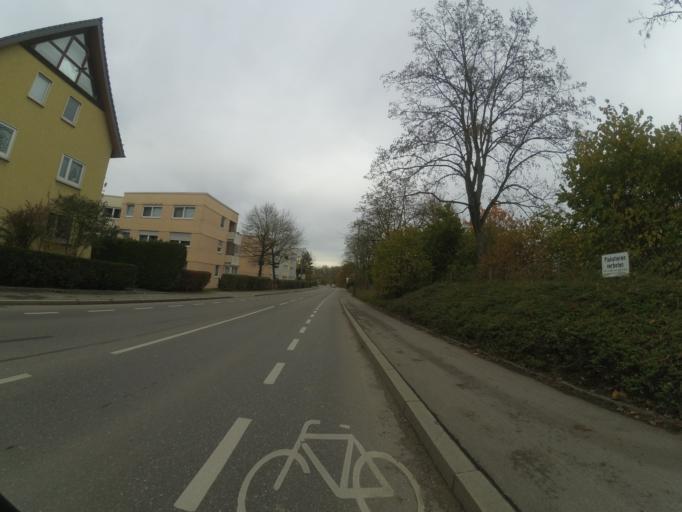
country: DE
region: Baden-Wuerttemberg
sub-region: Tuebingen Region
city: Ulm
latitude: 48.3628
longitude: 9.9897
